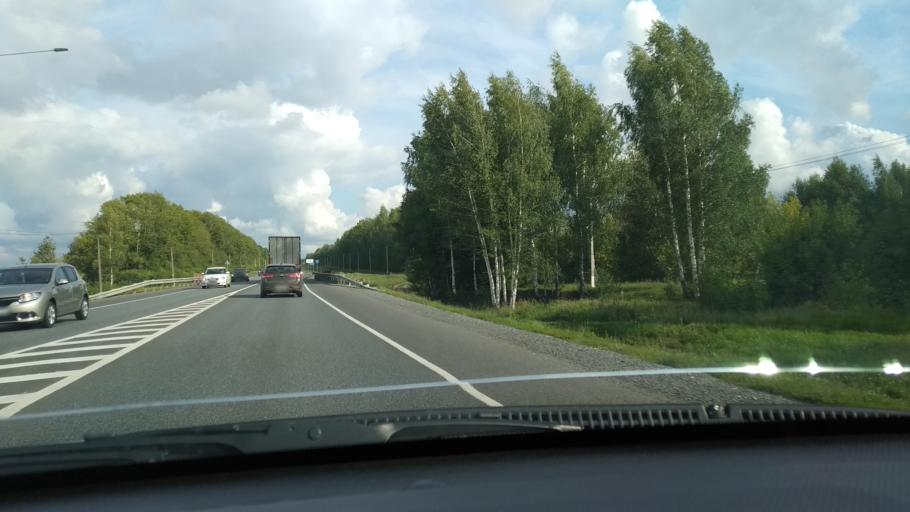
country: RU
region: Tatarstan
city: Stolbishchi
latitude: 55.6524
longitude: 49.3207
